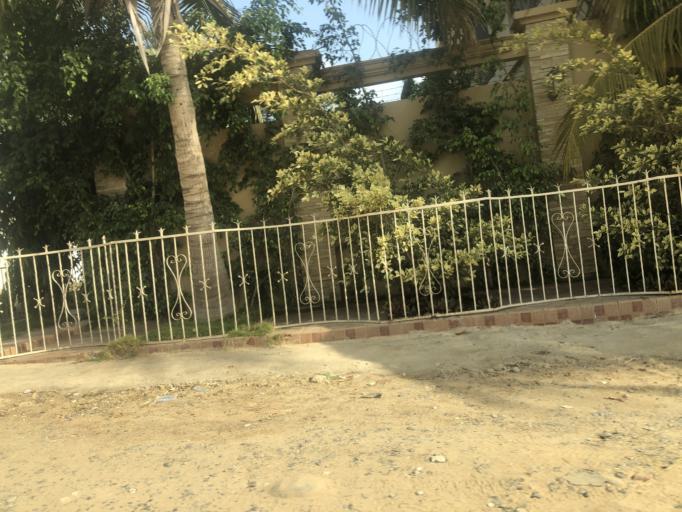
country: SN
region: Dakar
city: Mermoz Boabab
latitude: 14.7420
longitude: -17.5142
